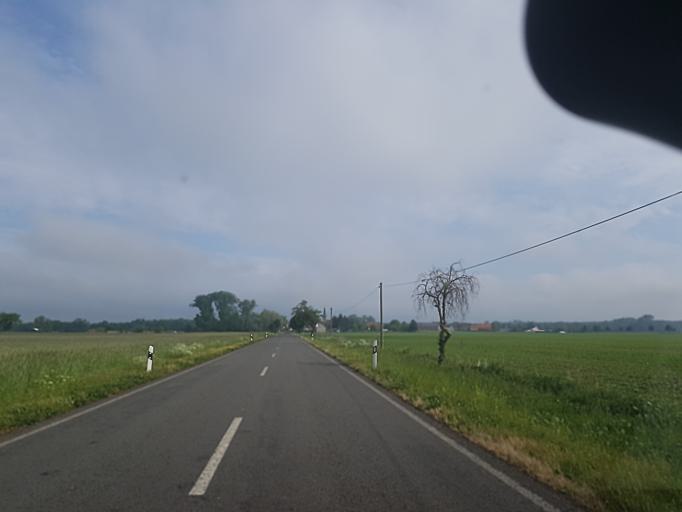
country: DE
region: Saxony-Anhalt
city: Rodleben
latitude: 52.0076
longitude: 12.2339
